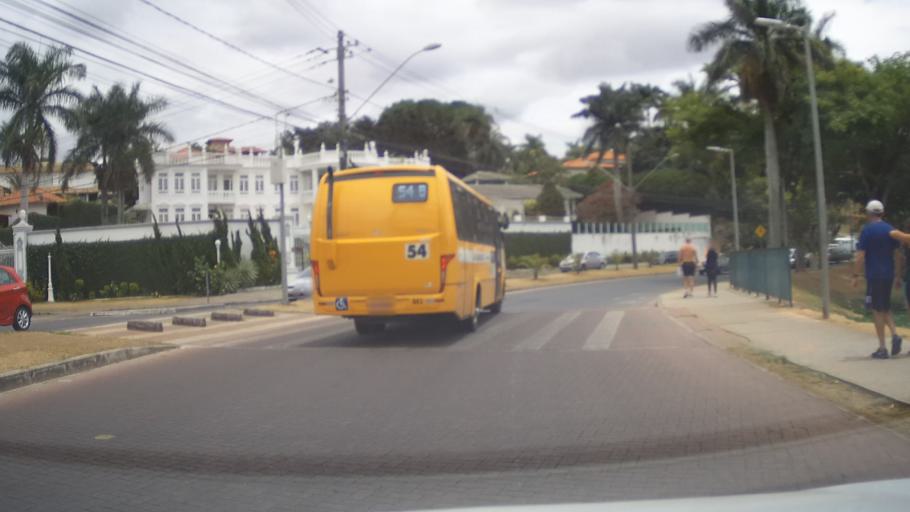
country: BR
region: Minas Gerais
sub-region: Belo Horizonte
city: Belo Horizonte
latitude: -19.8599
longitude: -43.9816
